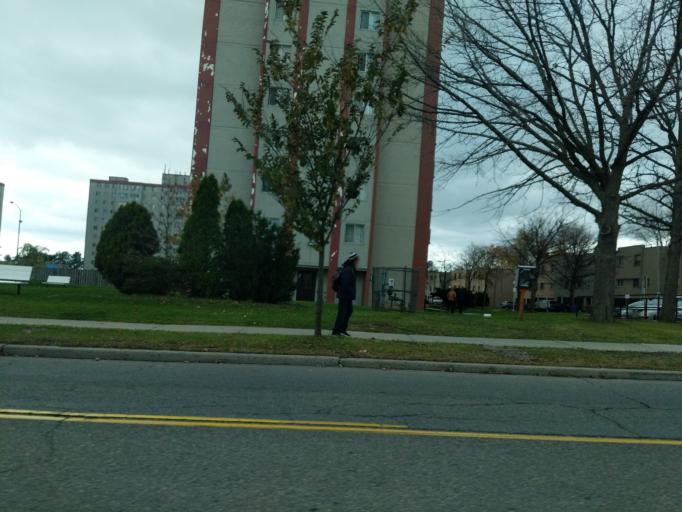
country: CA
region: Ontario
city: Toronto
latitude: 43.7072
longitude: -79.4656
